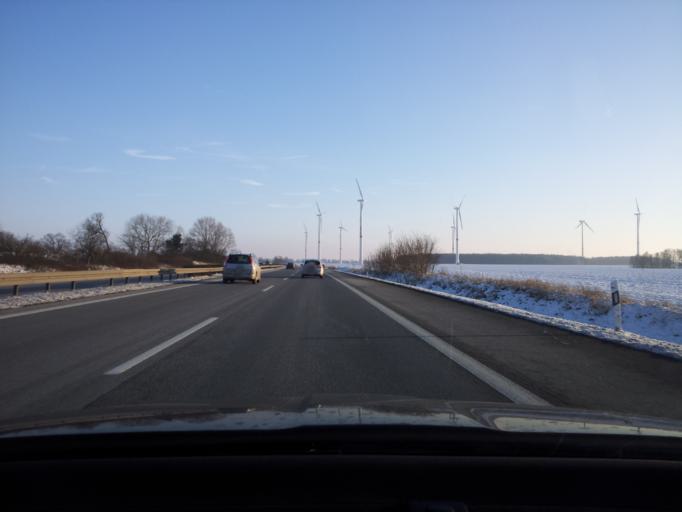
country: DE
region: Brandenburg
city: Heiligengrabe
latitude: 53.1926
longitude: 12.2806
